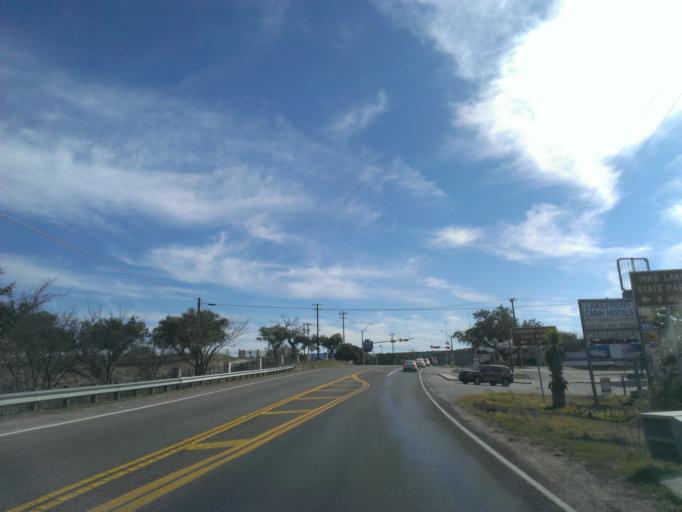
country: US
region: Texas
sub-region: Llano County
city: Kingsland
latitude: 30.6576
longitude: -98.4274
